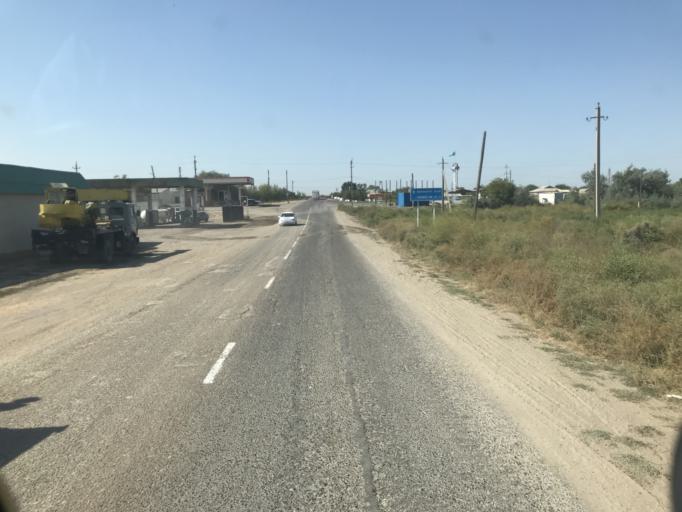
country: KZ
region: Ongtustik Qazaqstan
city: Myrzakent
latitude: 40.6706
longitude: 68.5522
